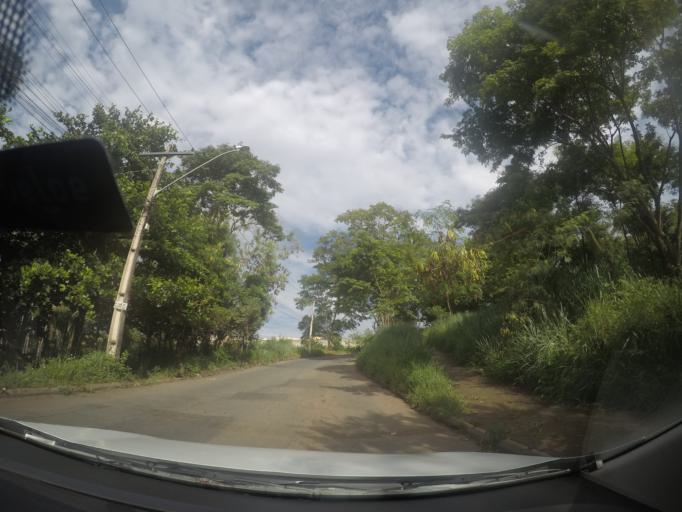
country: BR
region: Goias
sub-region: Goiania
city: Goiania
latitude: -16.6950
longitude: -49.1983
